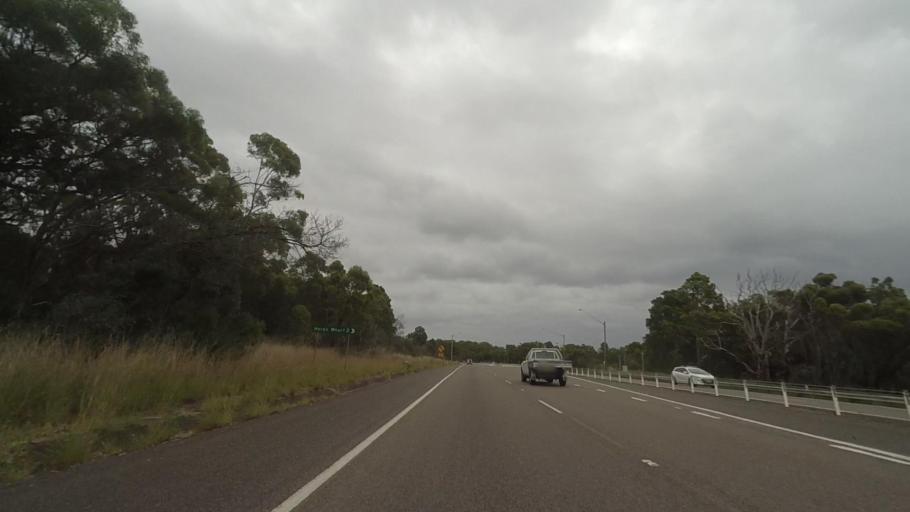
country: AU
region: New South Wales
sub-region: Wyong Shire
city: Kingfisher Shores
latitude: -33.1339
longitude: 151.6140
